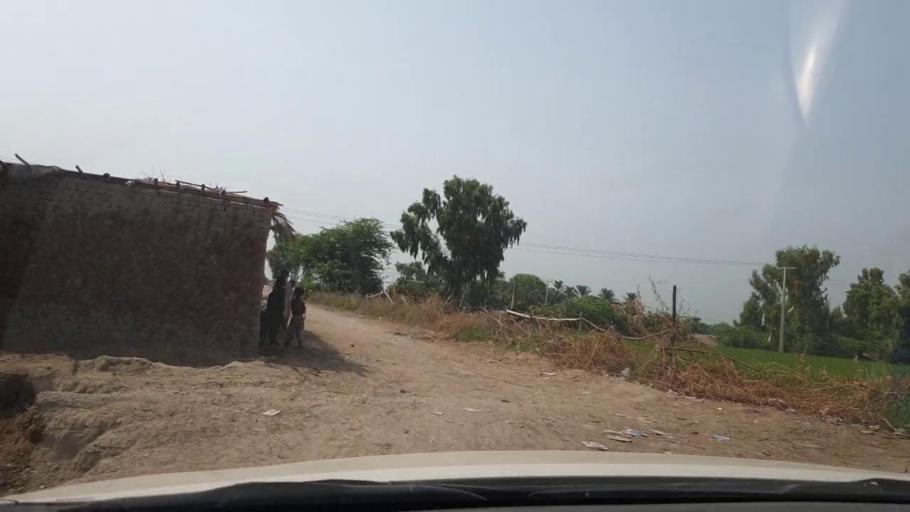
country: PK
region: Sindh
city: Shikarpur
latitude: 27.9744
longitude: 68.6769
